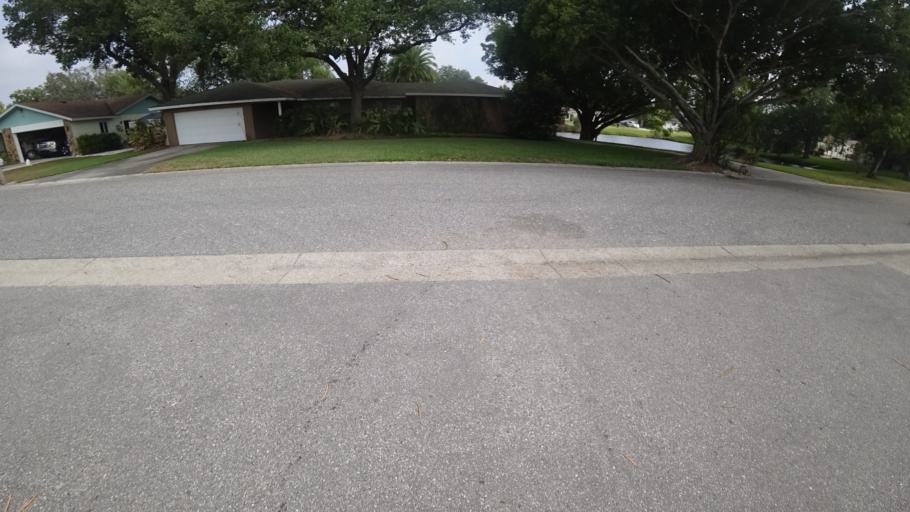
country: US
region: Florida
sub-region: Manatee County
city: West Bradenton
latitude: 27.4834
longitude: -82.6153
